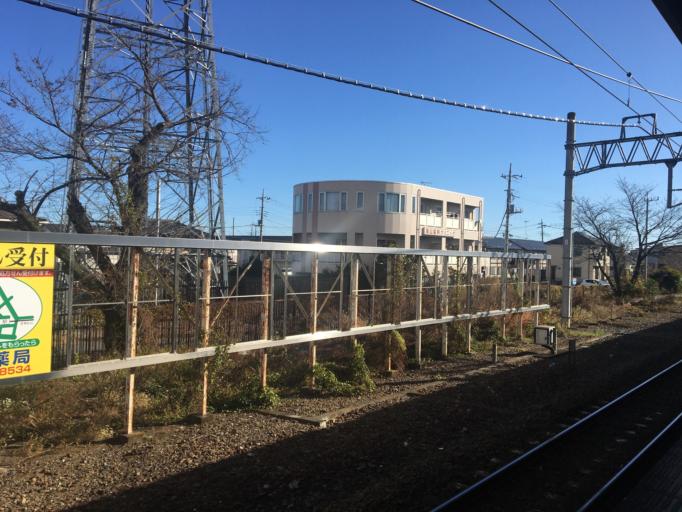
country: JP
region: Saitama
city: Ogawa
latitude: 36.0444
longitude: 139.3279
